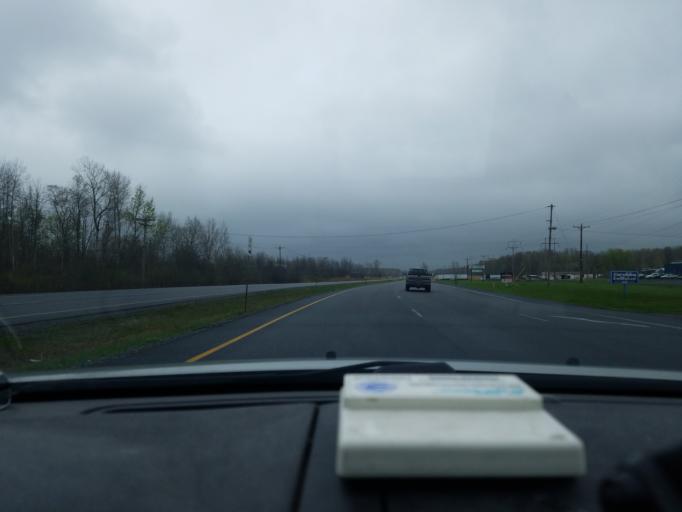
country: US
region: New York
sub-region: Onondaga County
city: North Syracuse
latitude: 43.1262
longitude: -76.0788
